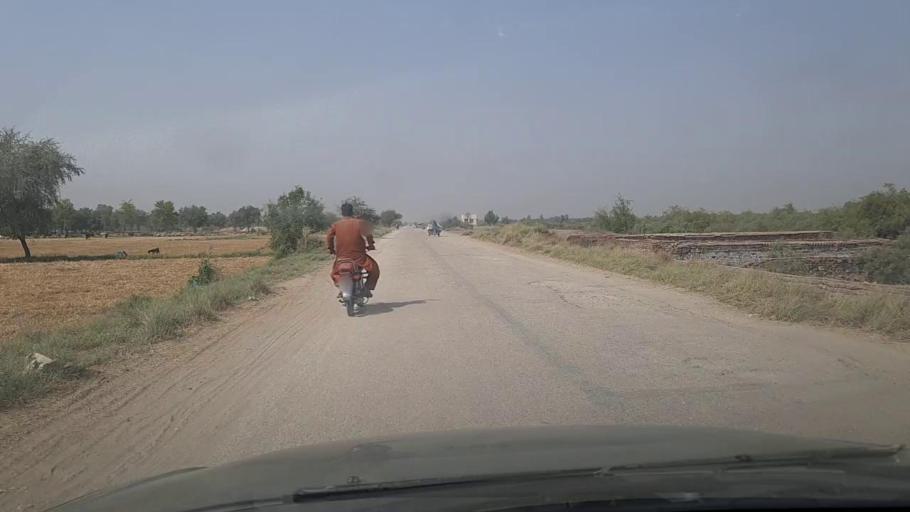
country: PK
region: Sindh
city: Mirpur Mathelo
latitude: 27.9131
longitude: 69.5170
